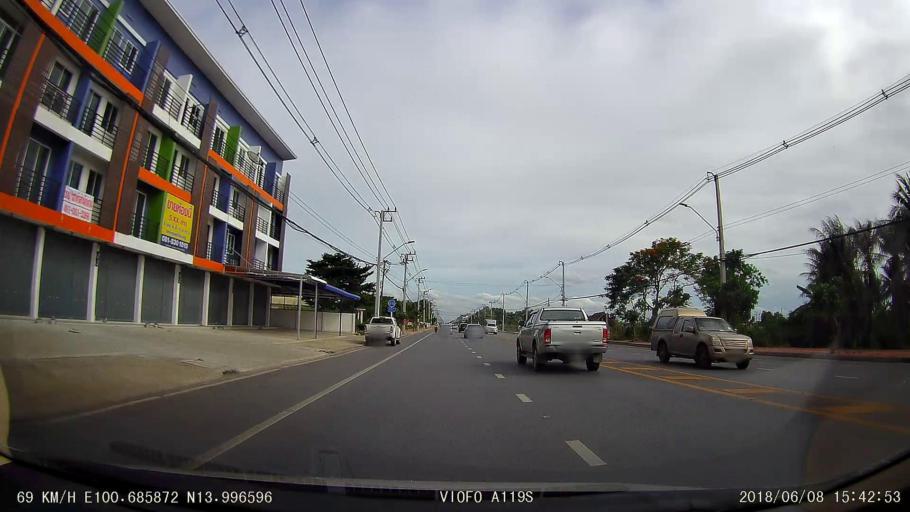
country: TH
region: Pathum Thani
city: Thanyaburi
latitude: 13.9964
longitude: 100.6859
